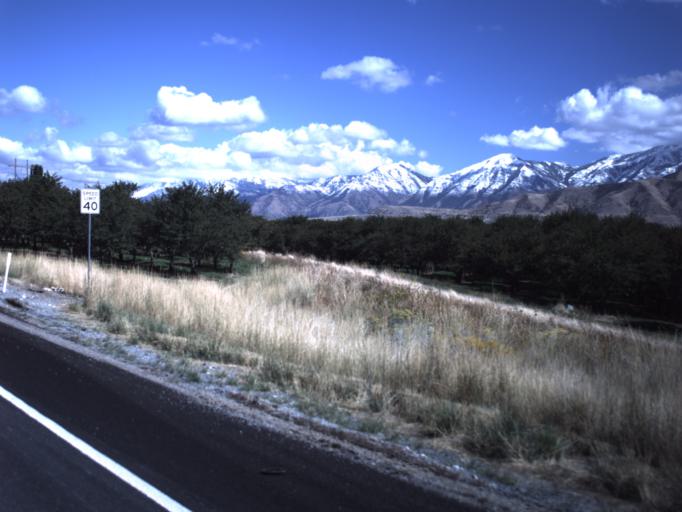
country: US
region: Utah
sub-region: Utah County
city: Santaquin
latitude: 40.0129
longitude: -111.8004
